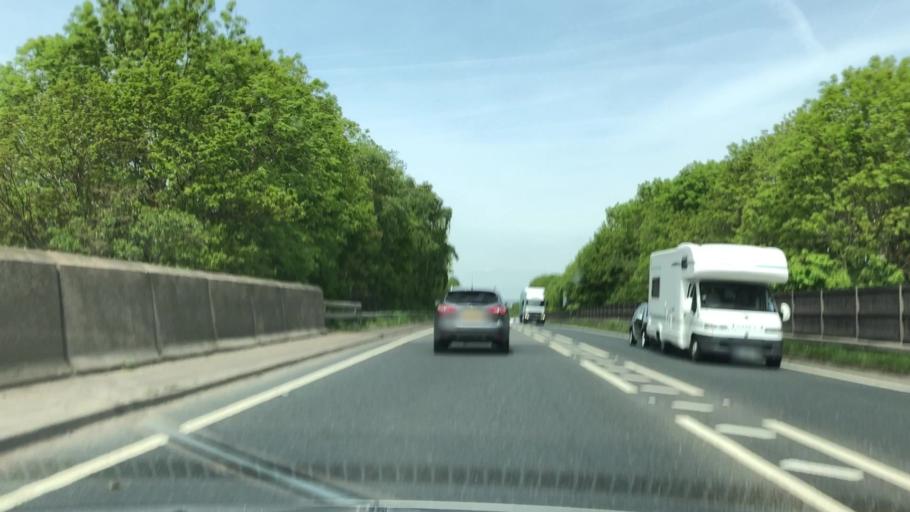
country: GB
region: England
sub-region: Shropshire
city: Gobowen
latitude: 52.9000
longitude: -3.0439
